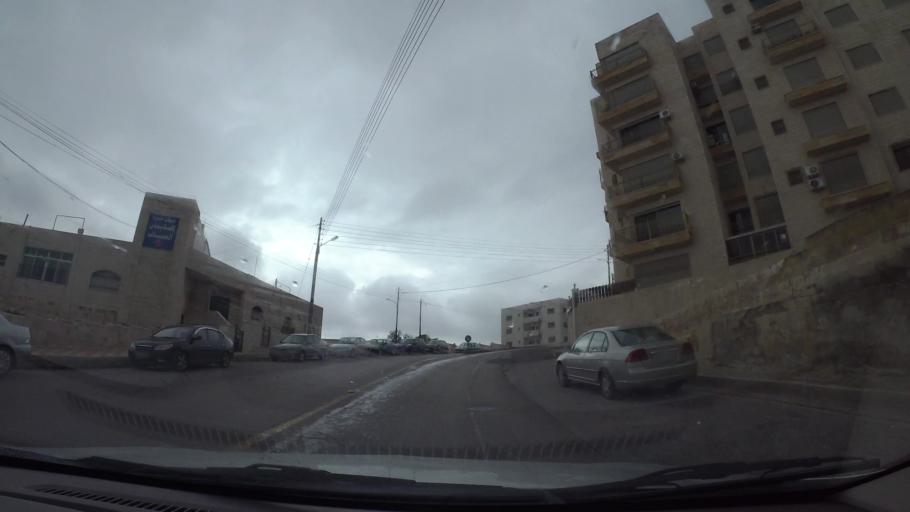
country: JO
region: Amman
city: Al Jubayhah
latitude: 31.9919
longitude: 35.8595
